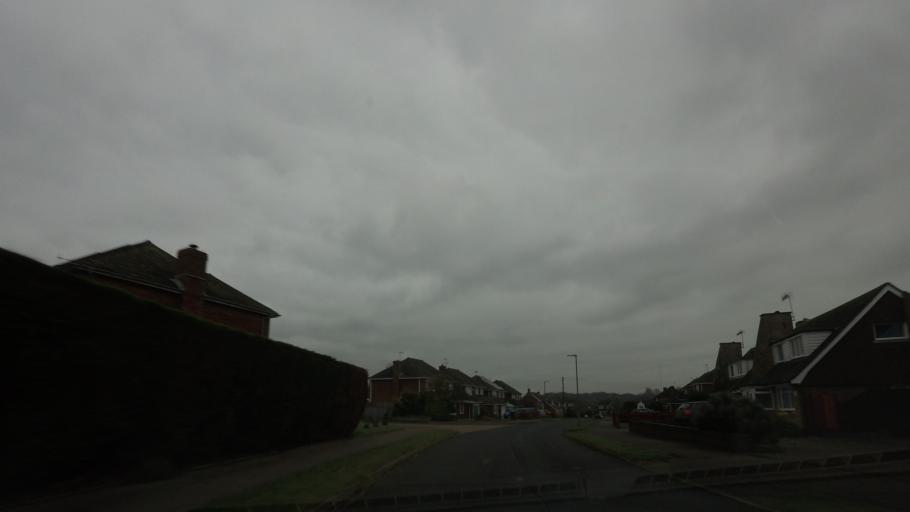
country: GB
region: England
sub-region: East Sussex
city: Bexhill-on-Sea
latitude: 50.8374
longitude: 0.4407
